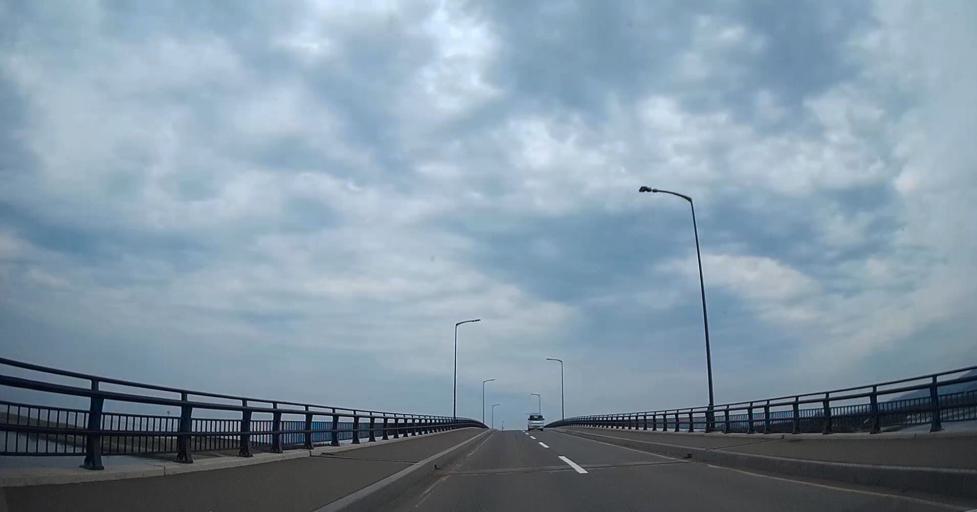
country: JP
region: Aomori
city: Shimokizukuri
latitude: 41.0383
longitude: 140.3268
